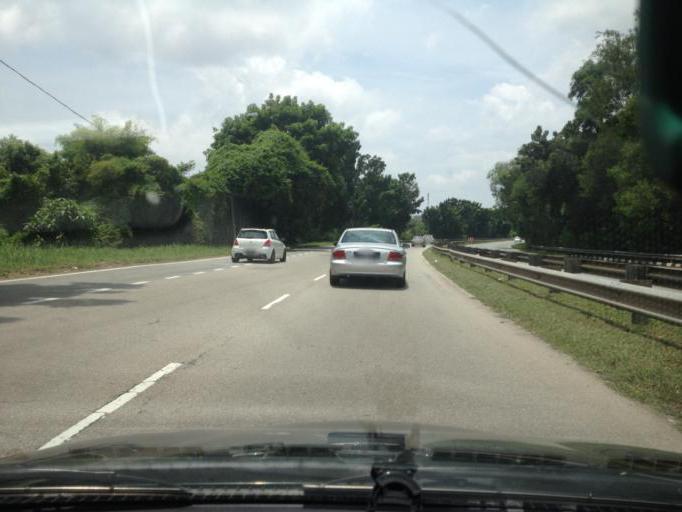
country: MY
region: Kedah
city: Sungai Petani
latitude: 5.6298
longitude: 100.5392
